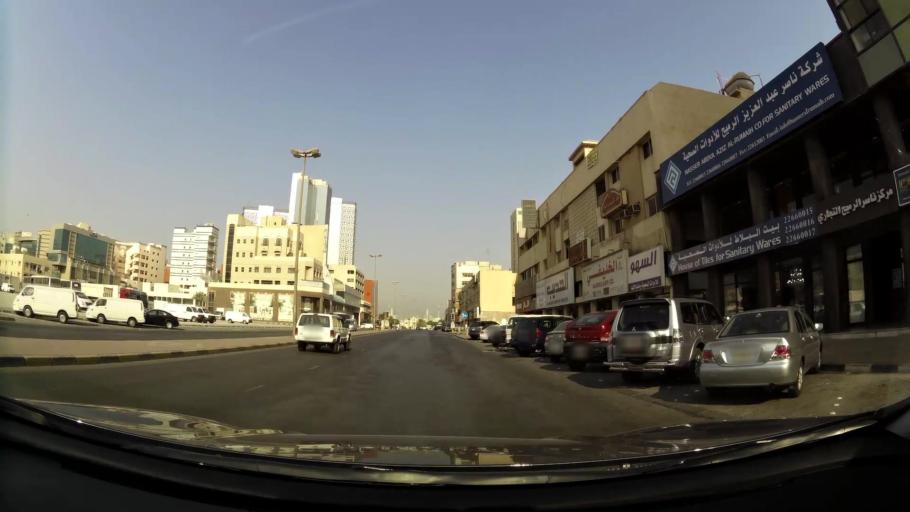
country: KW
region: Muhafazat Hawalli
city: Hawalli
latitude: 29.3456
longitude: 48.0148
